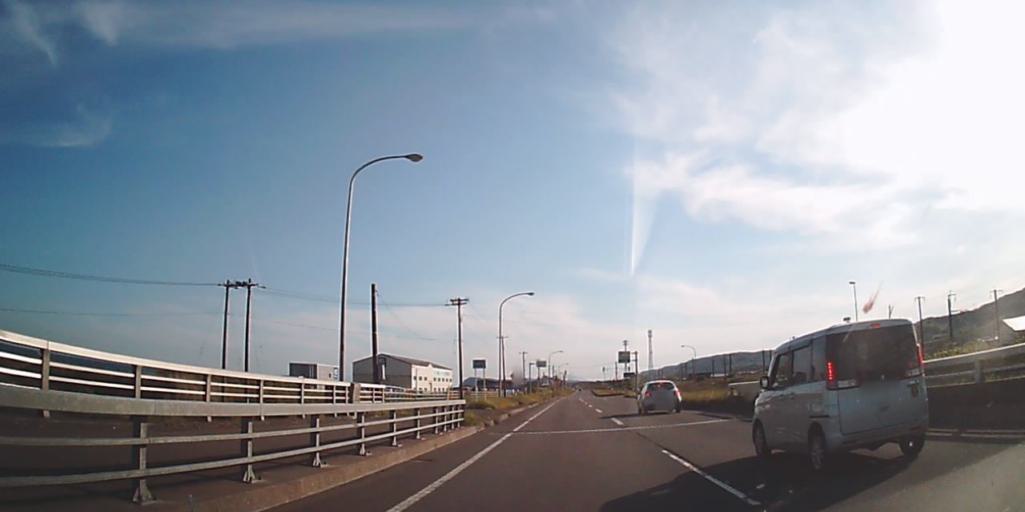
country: JP
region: Hokkaido
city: Muroran
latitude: 42.4037
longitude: 141.1004
